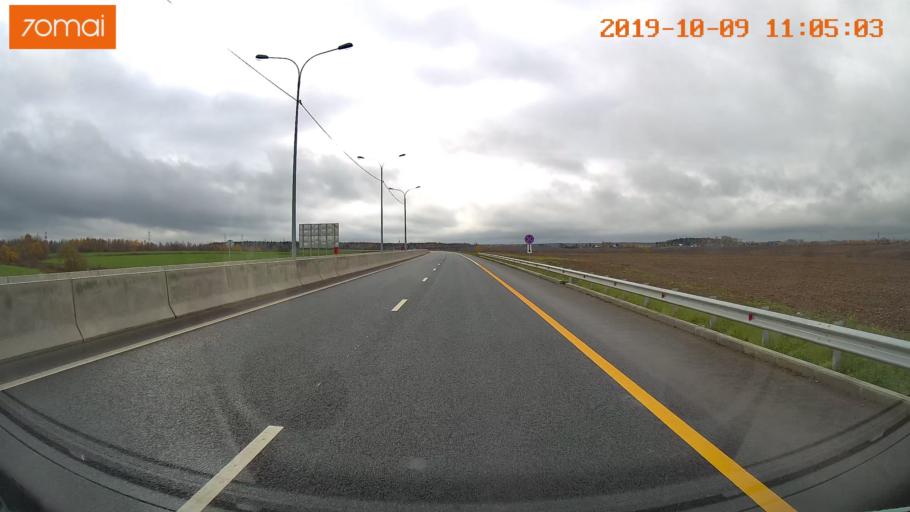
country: RU
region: Vologda
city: Molochnoye
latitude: 59.2048
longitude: 39.7605
